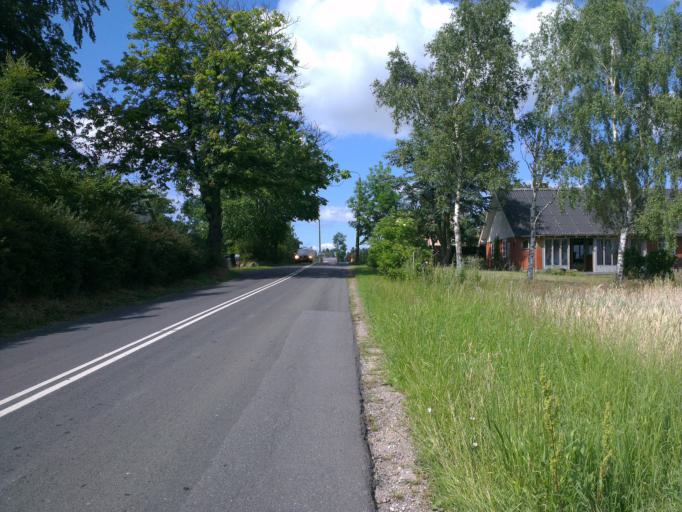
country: DK
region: Zealand
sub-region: Lejre Kommune
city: Ejby
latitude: 55.7422
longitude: 11.8816
